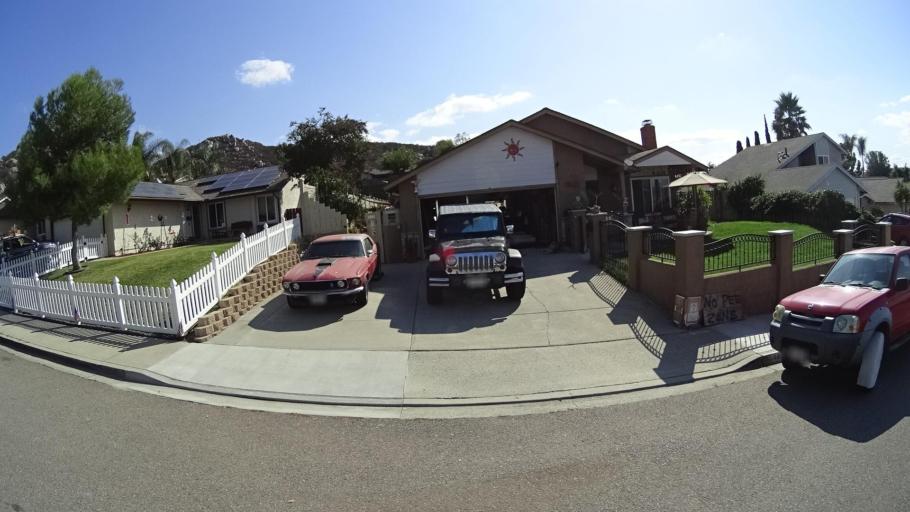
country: US
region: California
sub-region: San Diego County
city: Eucalyptus Hills
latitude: 32.8651
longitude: -116.9584
